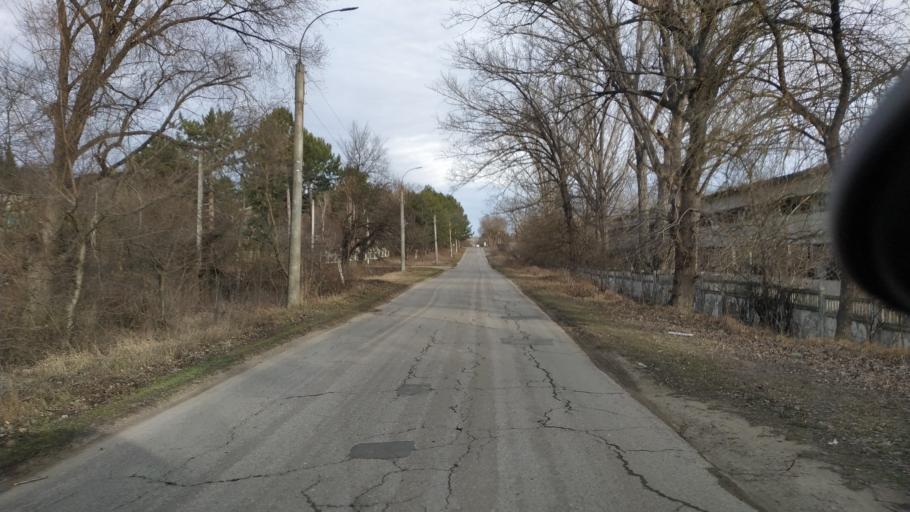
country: MD
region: Chisinau
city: Vadul lui Voda
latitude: 47.1004
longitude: 29.0683
